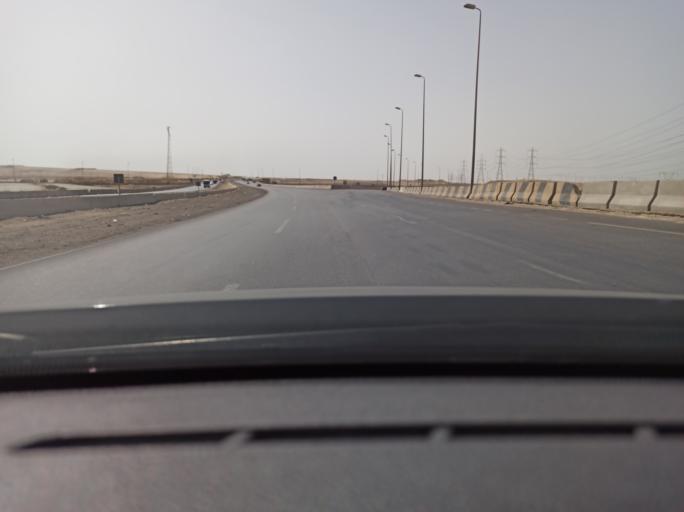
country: EG
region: Muhafazat al Qahirah
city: Halwan
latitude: 29.7216
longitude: 31.4052
